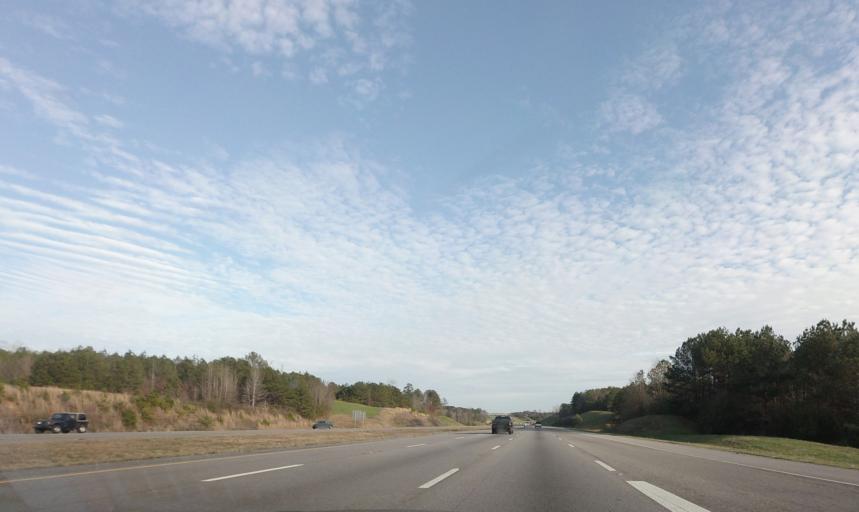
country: US
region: Alabama
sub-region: Walker County
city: Cordova
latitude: 33.7175
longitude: -87.1746
